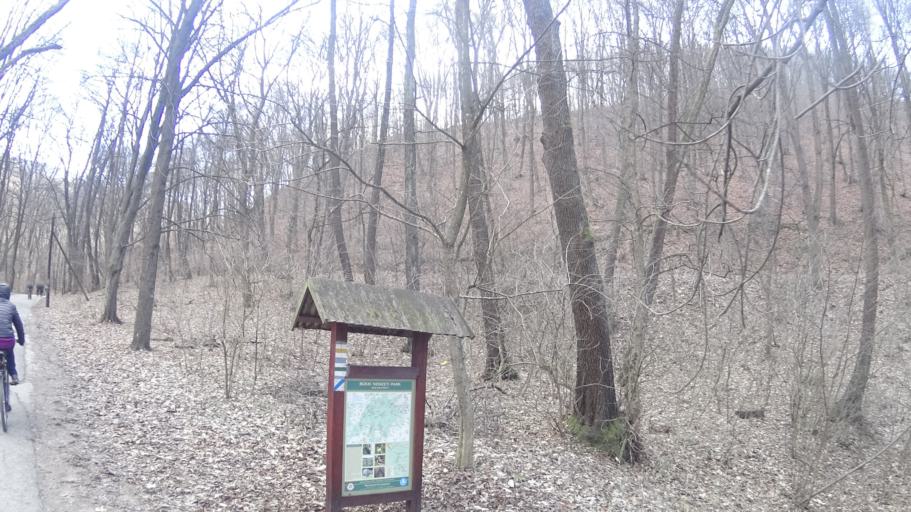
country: HU
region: Heves
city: Szilvasvarad
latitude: 48.0894
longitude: 20.4037
